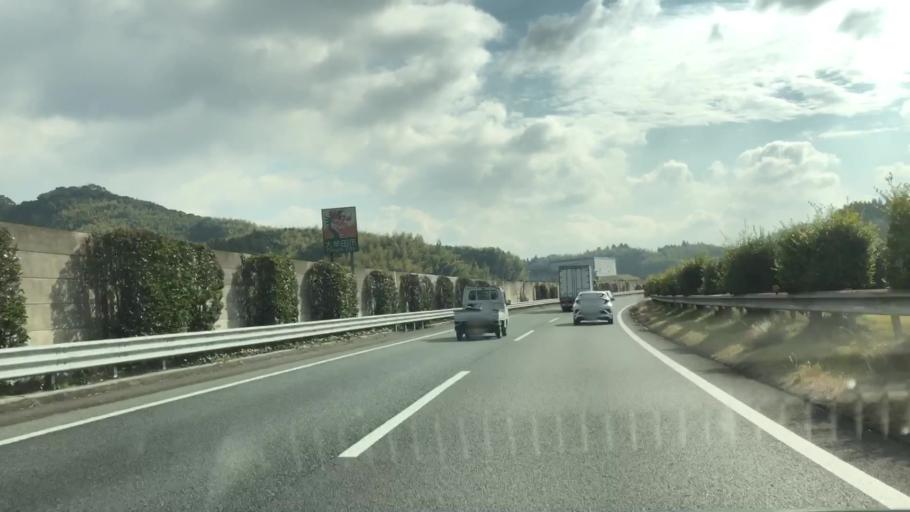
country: JP
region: Fukuoka
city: Setakamachi-takayanagi
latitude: 33.0855
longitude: 130.5413
